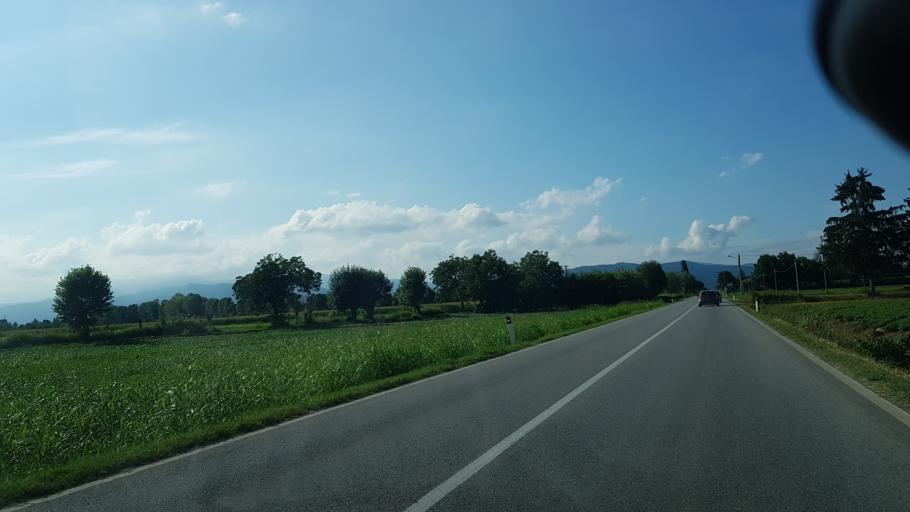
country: IT
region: Piedmont
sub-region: Provincia di Cuneo
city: Roata Rossi
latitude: 44.4617
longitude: 7.5179
